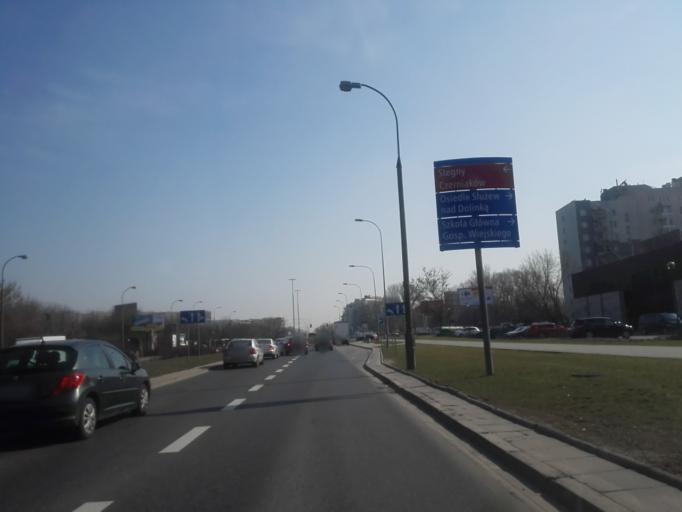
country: PL
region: Masovian Voivodeship
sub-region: Warszawa
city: Mokotow
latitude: 52.1760
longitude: 21.0406
